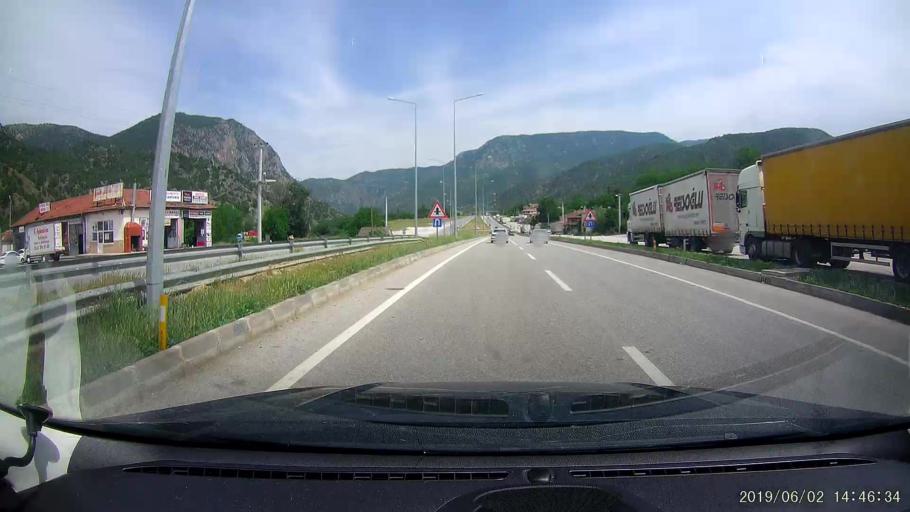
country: TR
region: Corum
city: Hacihamza
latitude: 41.0761
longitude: 34.4506
